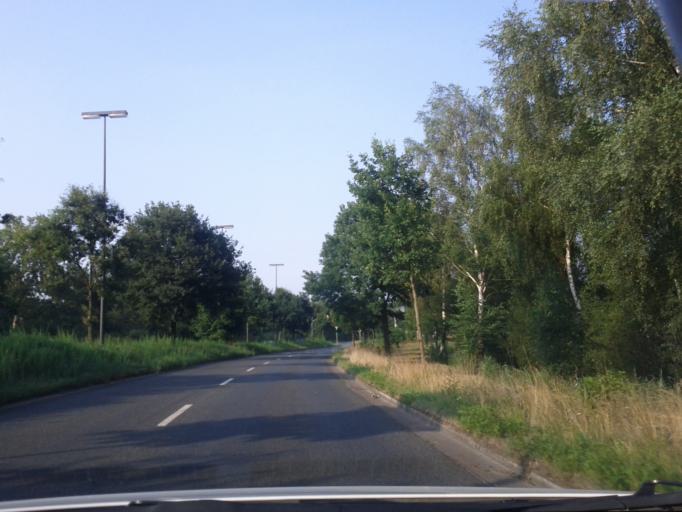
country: DE
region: Bremen
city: Bremen
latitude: 53.1041
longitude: 8.8565
